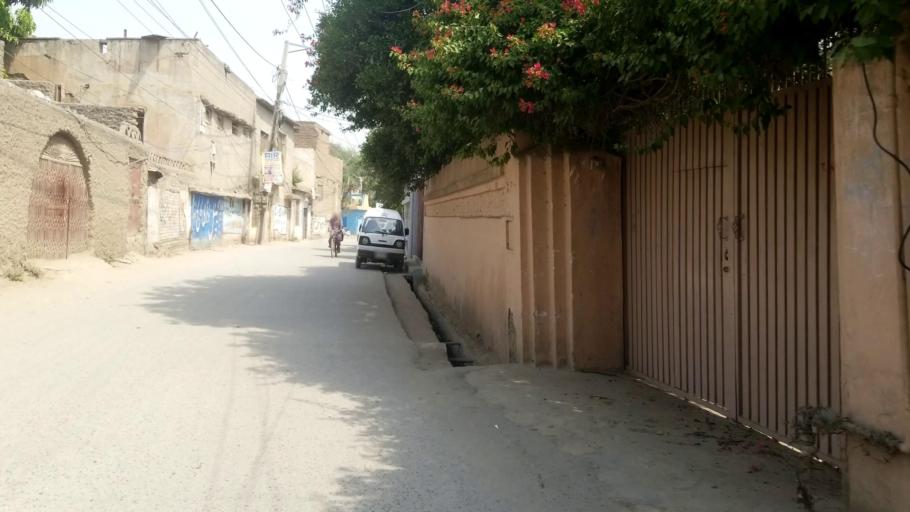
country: PK
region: Khyber Pakhtunkhwa
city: Peshawar
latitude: 33.9876
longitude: 71.5334
